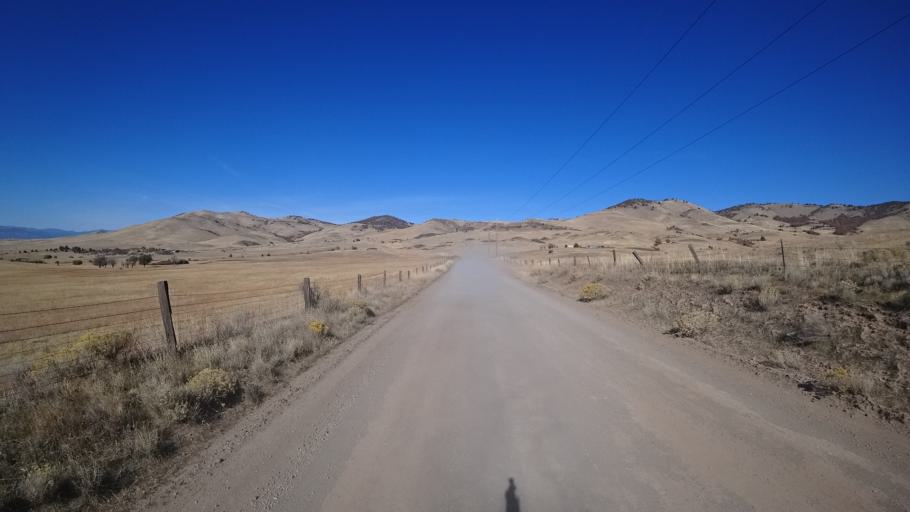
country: US
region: California
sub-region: Siskiyou County
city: Montague
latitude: 41.8245
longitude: -122.3623
